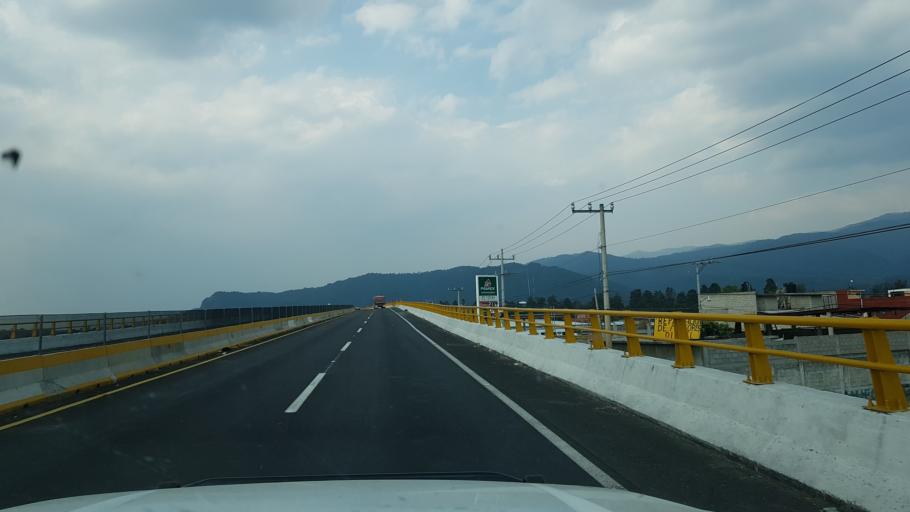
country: MX
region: Mexico
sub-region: Ayapango
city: La Colonia
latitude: 19.1362
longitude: -98.7771
